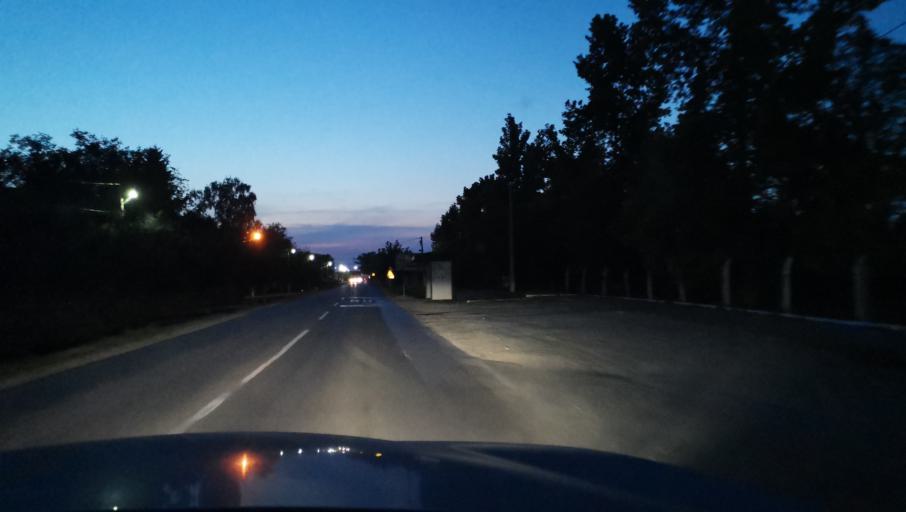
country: RS
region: Central Serbia
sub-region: Belgrade
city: Surcin
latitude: 44.7621
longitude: 20.2517
